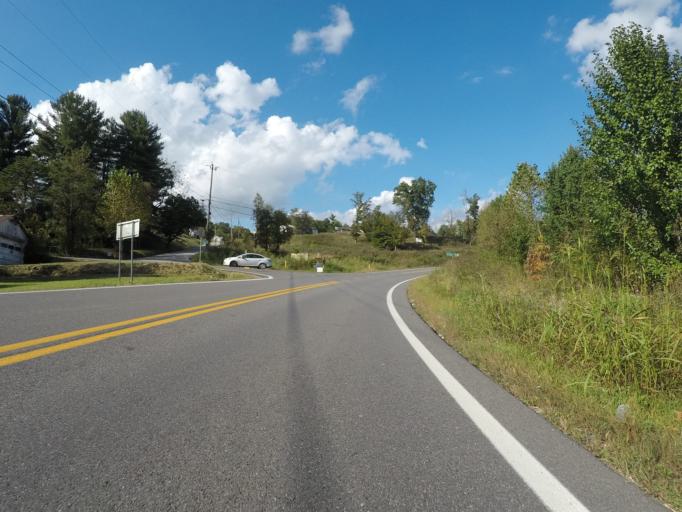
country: US
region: Ohio
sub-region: Lawrence County
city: Burlington
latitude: 38.3761
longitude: -82.5315
